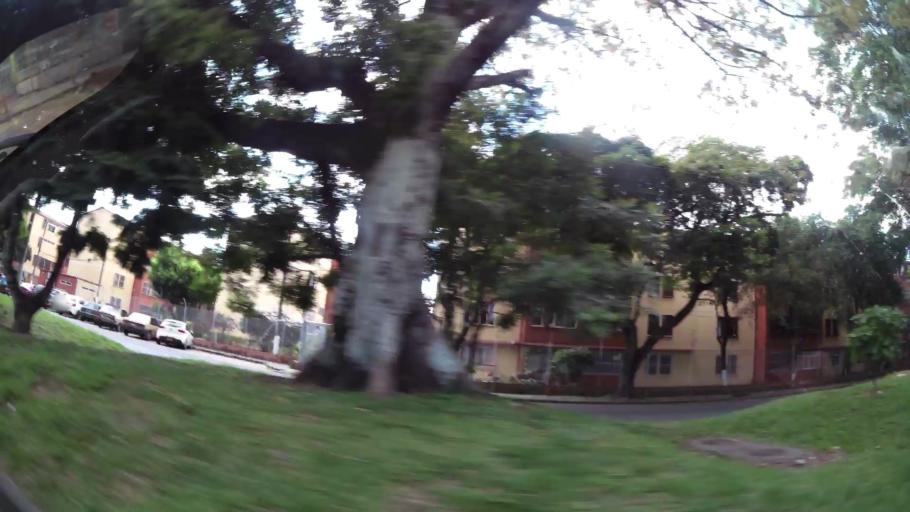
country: CO
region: Valle del Cauca
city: Cali
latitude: 3.4114
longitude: -76.5292
